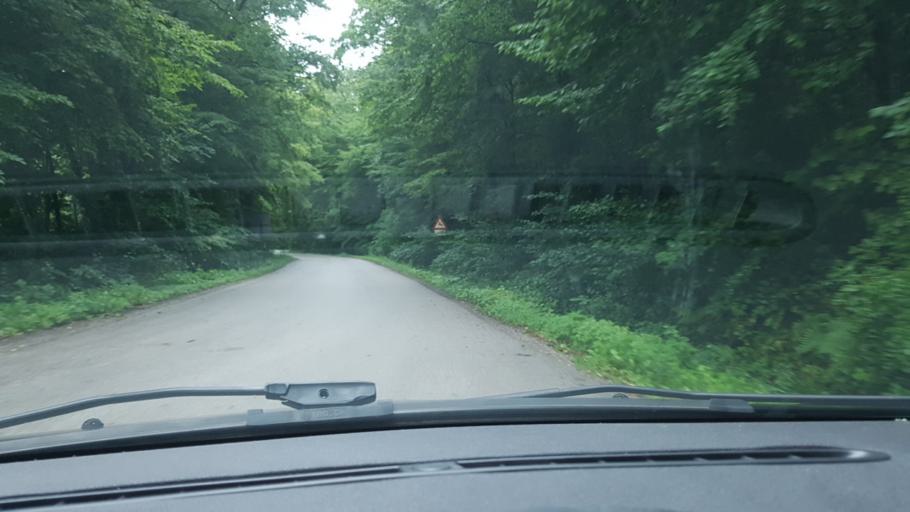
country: HR
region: Karlovacka
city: Ozalj
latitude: 45.6252
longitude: 15.5222
